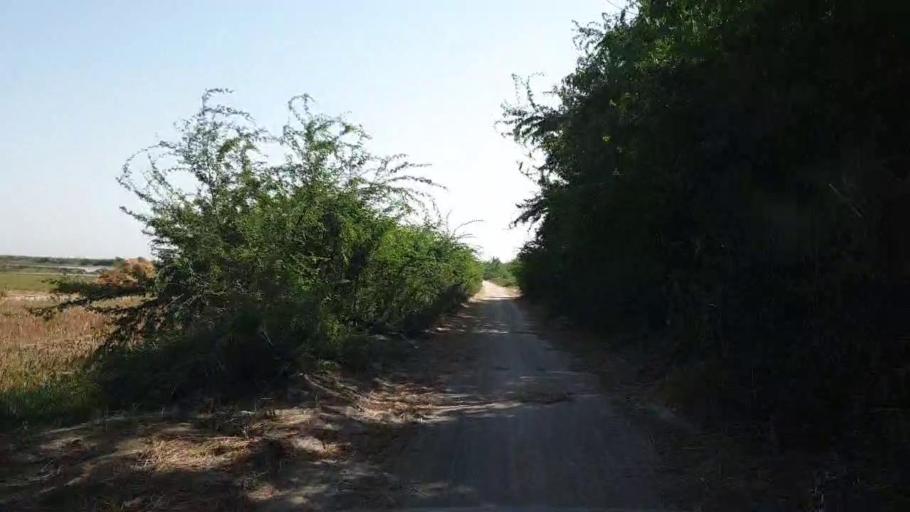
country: PK
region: Sindh
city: Tando Bago
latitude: 24.6482
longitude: 68.9850
